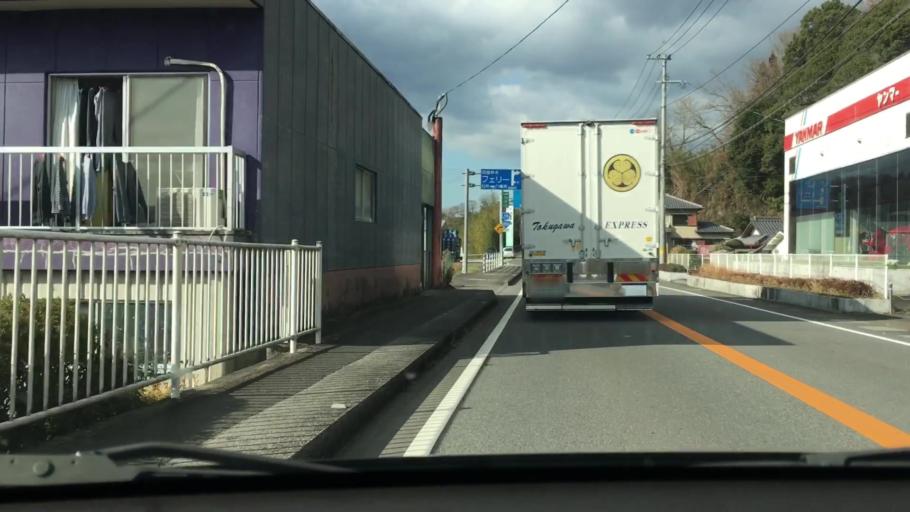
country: JP
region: Oita
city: Usuki
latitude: 33.0489
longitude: 131.6900
